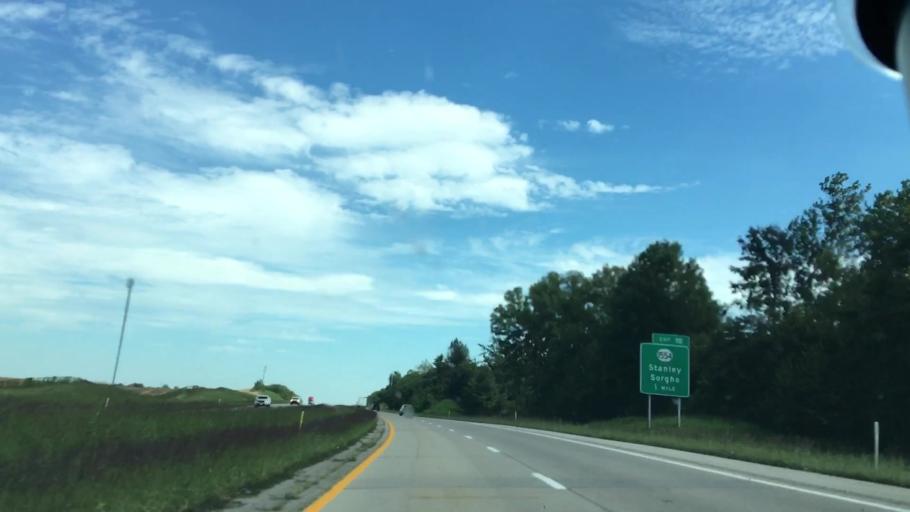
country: US
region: Kentucky
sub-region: Daviess County
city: Owensboro
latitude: 37.7513
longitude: -87.2844
